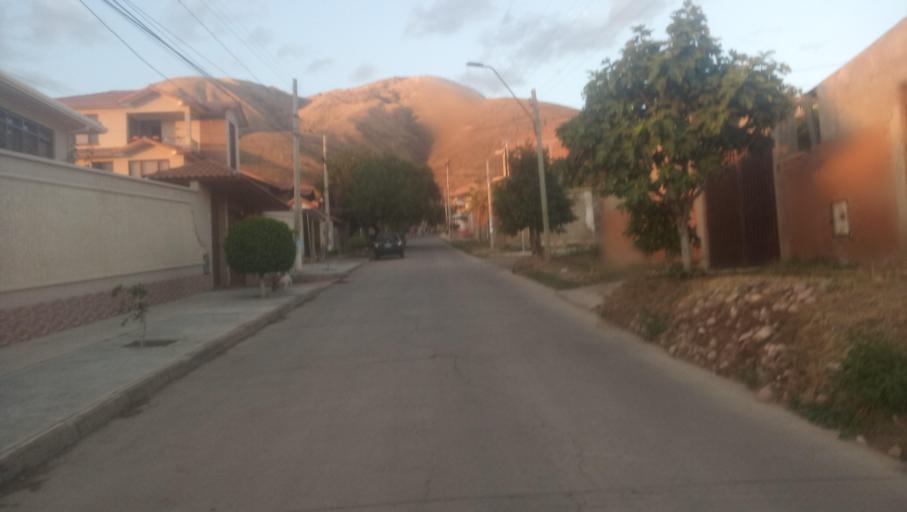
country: BO
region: Cochabamba
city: Cochabamba
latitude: -17.3738
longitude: -66.0950
